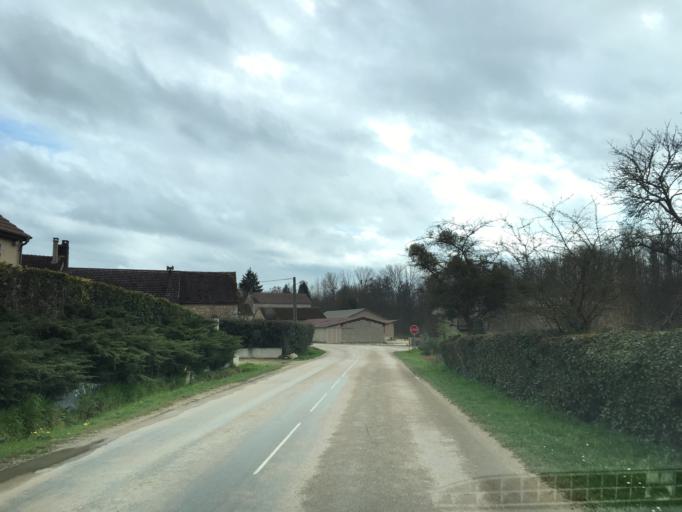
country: FR
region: Bourgogne
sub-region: Departement de l'Yonne
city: Pourrain
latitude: 47.7964
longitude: 3.3829
